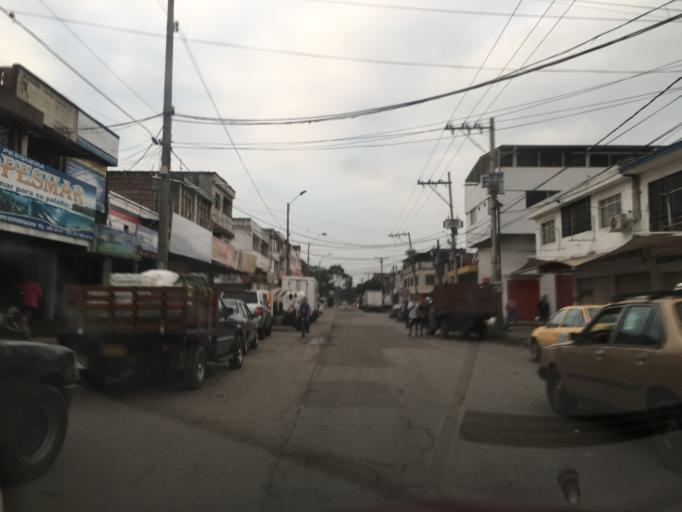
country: CO
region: Valle del Cauca
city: Cali
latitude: 3.4256
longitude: -76.5213
